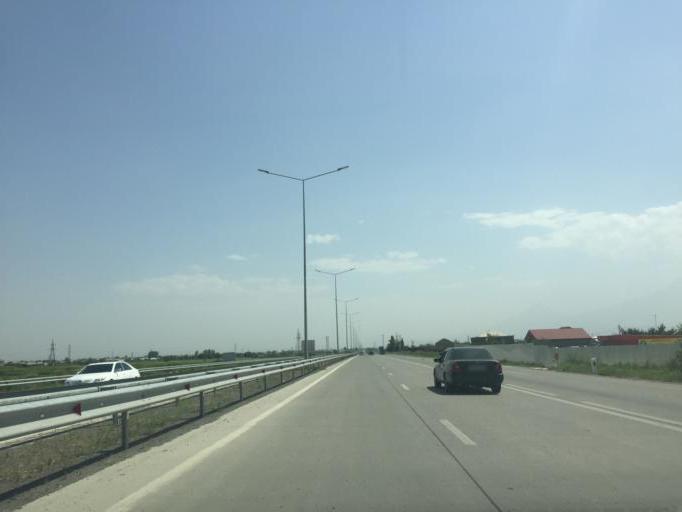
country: AM
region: Ararat
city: Masis
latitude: 40.0759
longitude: 44.4542
